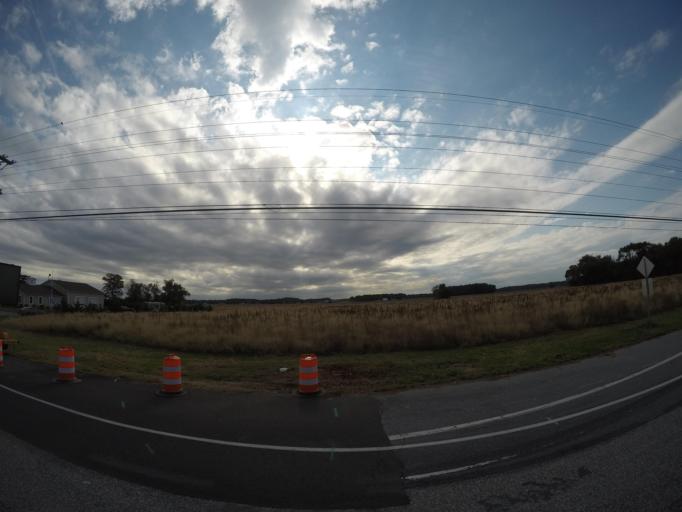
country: US
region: Delaware
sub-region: Sussex County
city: Lewes
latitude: 38.7260
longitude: -75.1448
